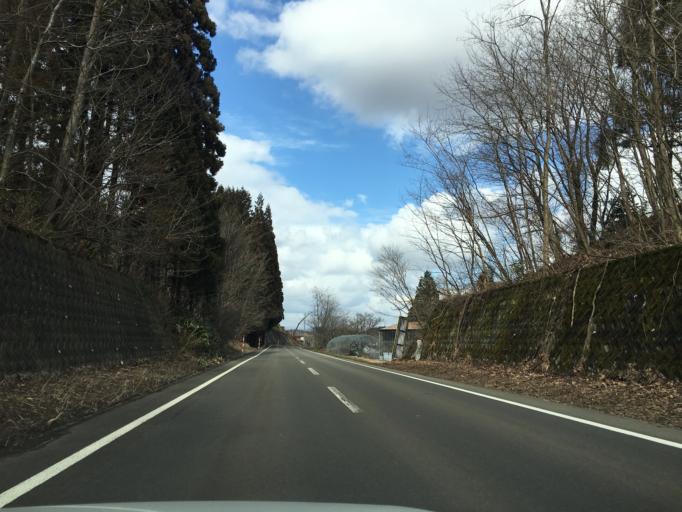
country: JP
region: Akita
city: Odate
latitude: 40.1969
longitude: 140.5348
